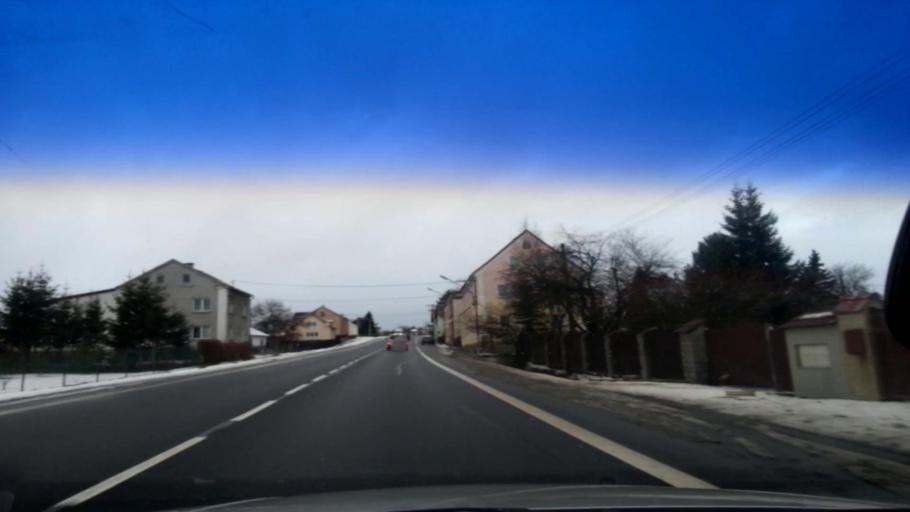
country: CZ
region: Karlovarsky
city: Hazlov
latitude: 50.1580
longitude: 12.2716
